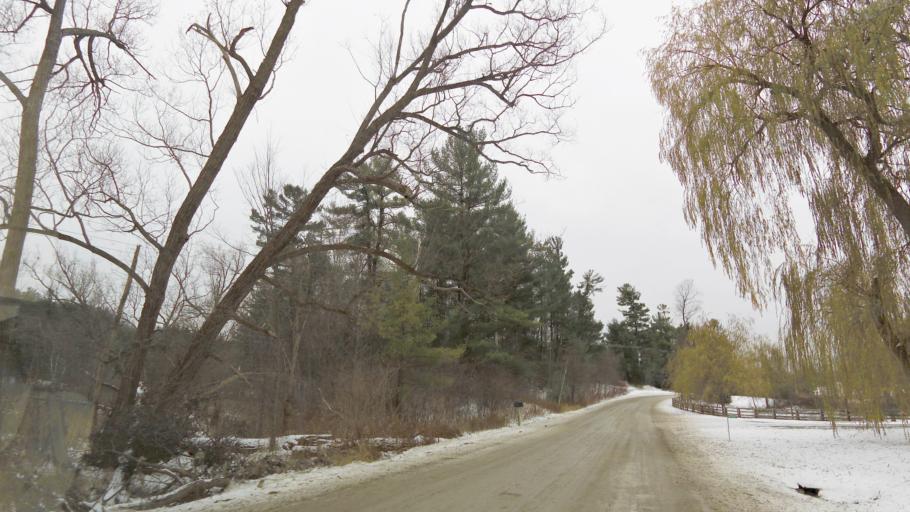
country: CA
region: Ontario
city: Vaughan
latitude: 43.9488
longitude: -79.6183
